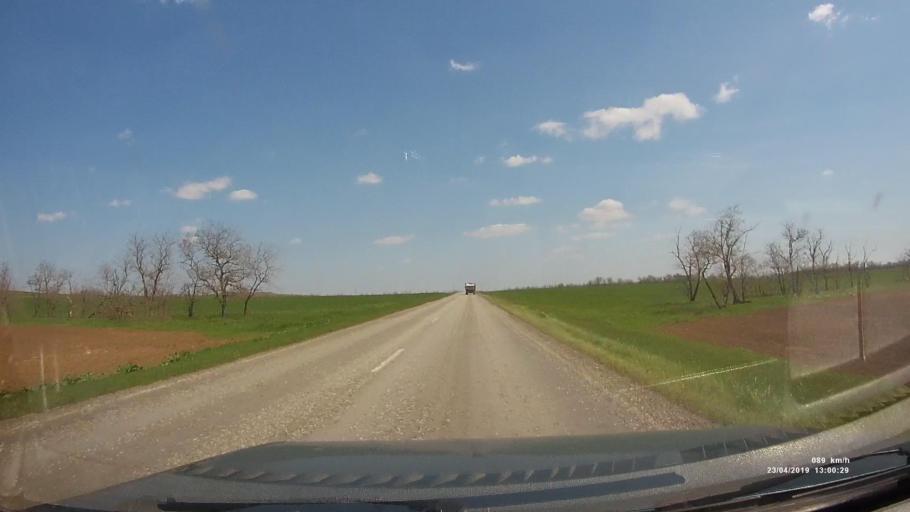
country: RU
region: Kalmykiya
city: Yashalta
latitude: 46.6041
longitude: 42.6353
